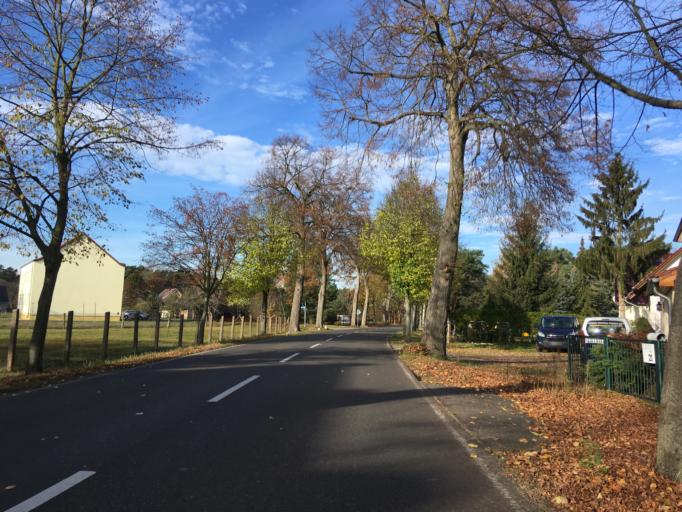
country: DE
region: Brandenburg
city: Gross Koris
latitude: 52.1496
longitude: 13.6815
